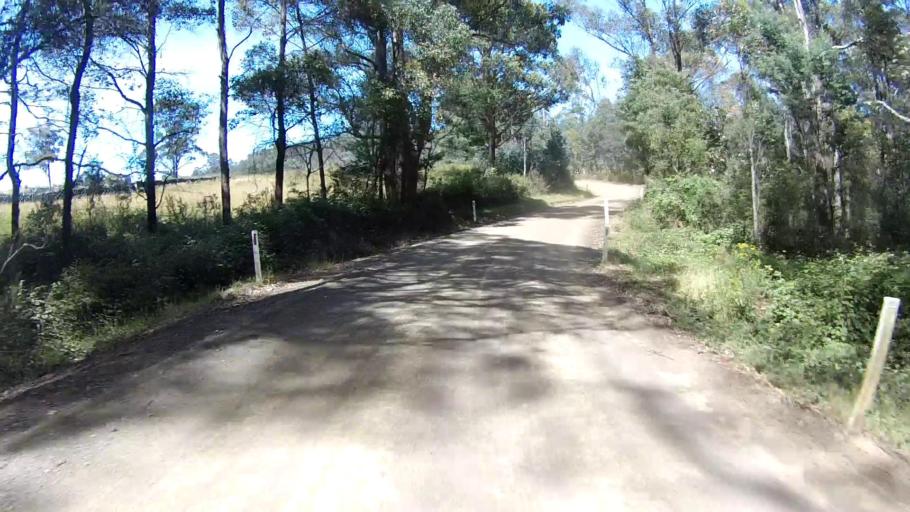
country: AU
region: Tasmania
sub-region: Sorell
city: Sorell
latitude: -42.7020
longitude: 147.7432
